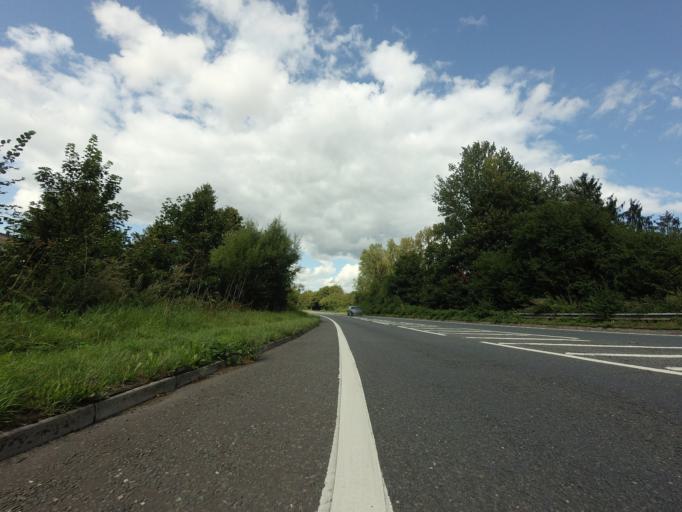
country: GB
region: England
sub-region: Kent
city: Borough Green
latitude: 51.2868
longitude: 0.2826
